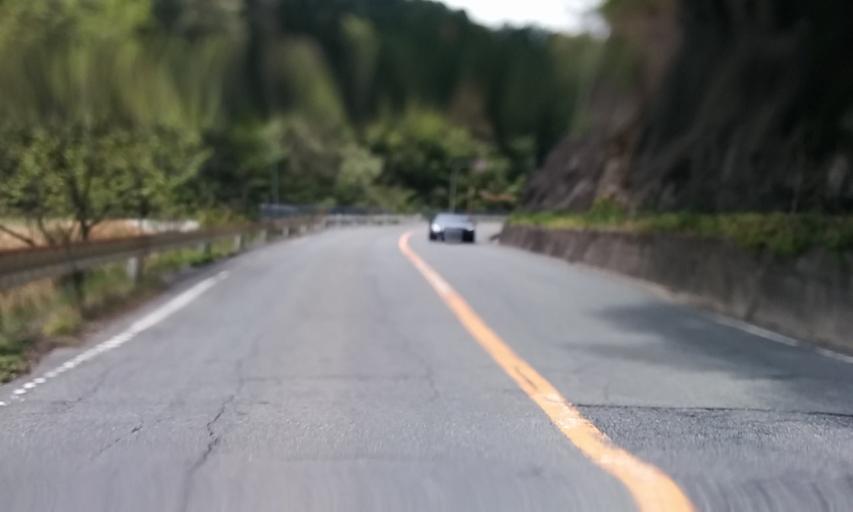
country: JP
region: Kyoto
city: Kameoka
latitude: 34.9697
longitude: 135.5842
